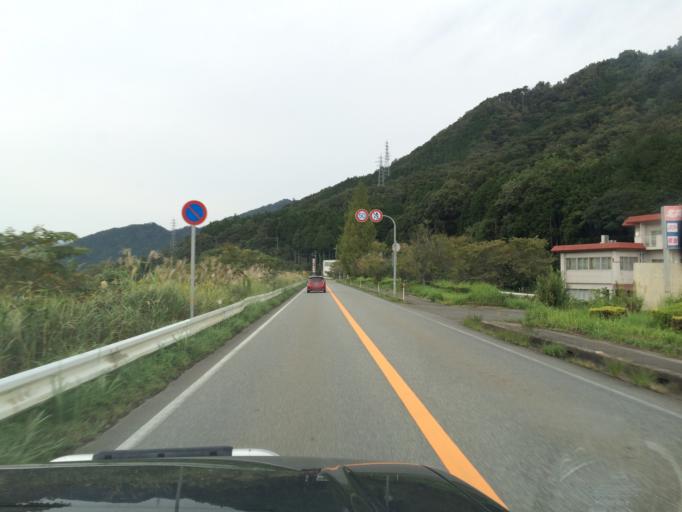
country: JP
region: Hyogo
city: Toyooka
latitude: 35.3867
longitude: 134.8153
